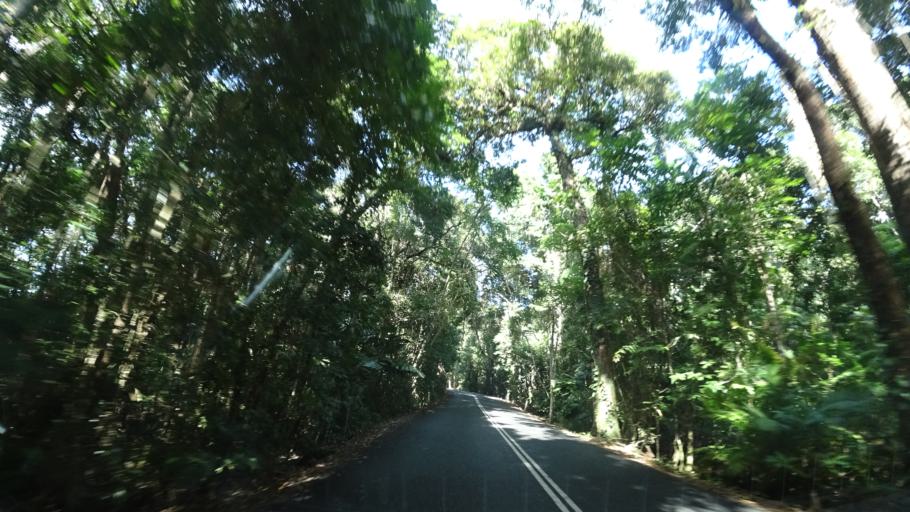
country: AU
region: Queensland
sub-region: Cairns
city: Port Douglas
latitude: -16.1353
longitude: 145.4511
